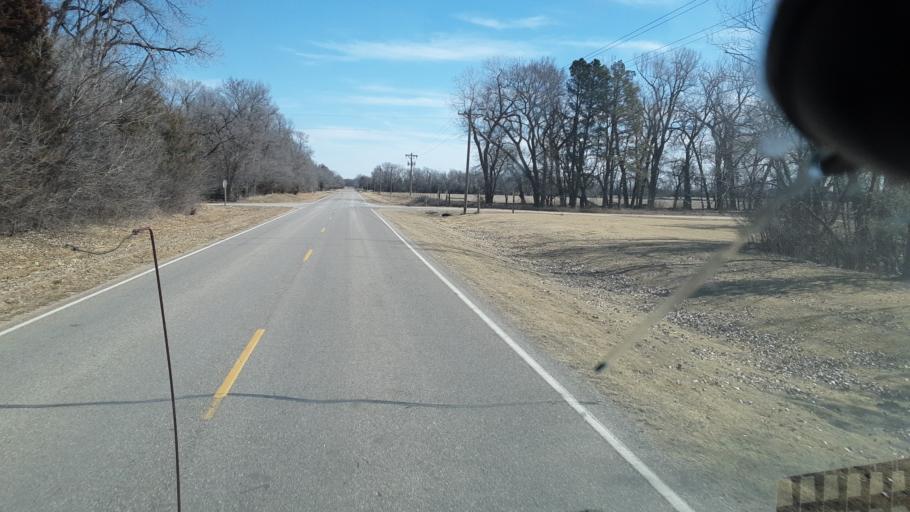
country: US
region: Kansas
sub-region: Reno County
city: Buhler
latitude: 38.1593
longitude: -97.8682
